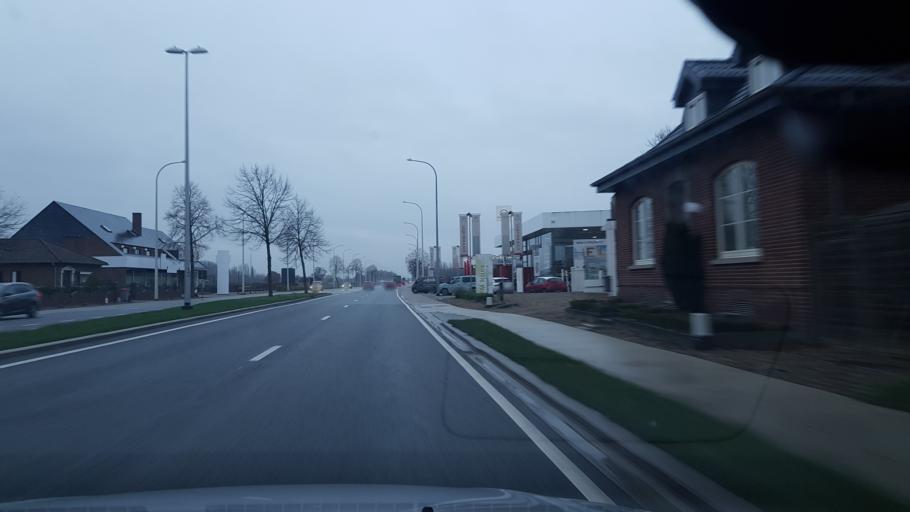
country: BE
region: Flanders
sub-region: Provincie Limburg
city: Maasmechelen
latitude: 50.9381
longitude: 5.6915
